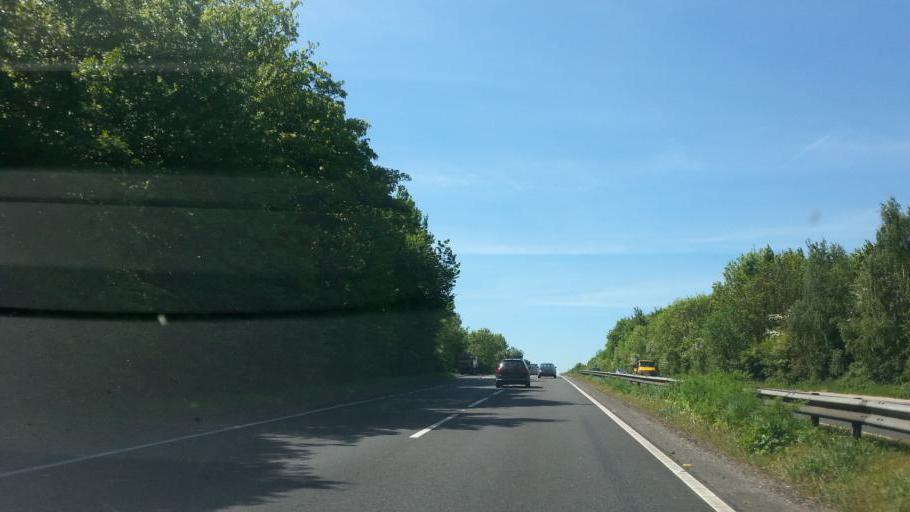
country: GB
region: England
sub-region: Hampshire
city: Andover
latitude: 51.1974
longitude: -1.4958
